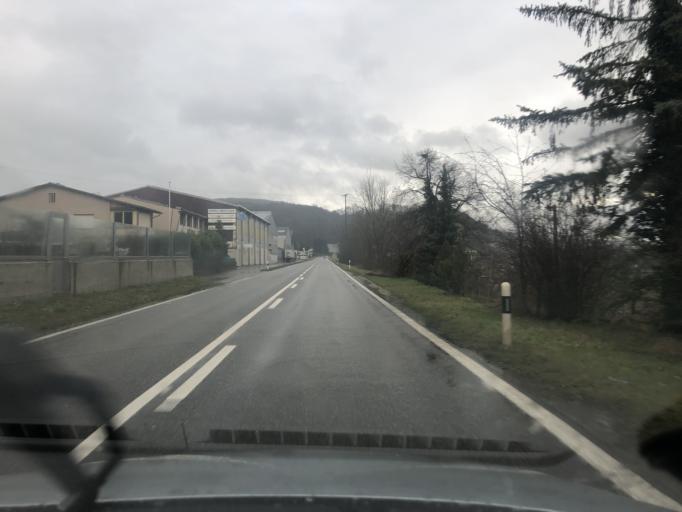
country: CH
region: Aargau
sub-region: Bezirk Zurzach
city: Koblenz
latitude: 47.5950
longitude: 8.2329
